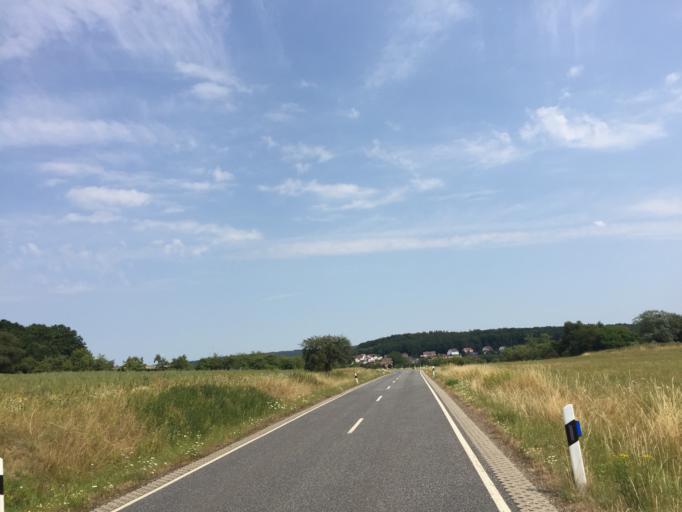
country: DE
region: Hesse
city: Staufenberg
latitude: 50.6399
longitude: 8.7321
